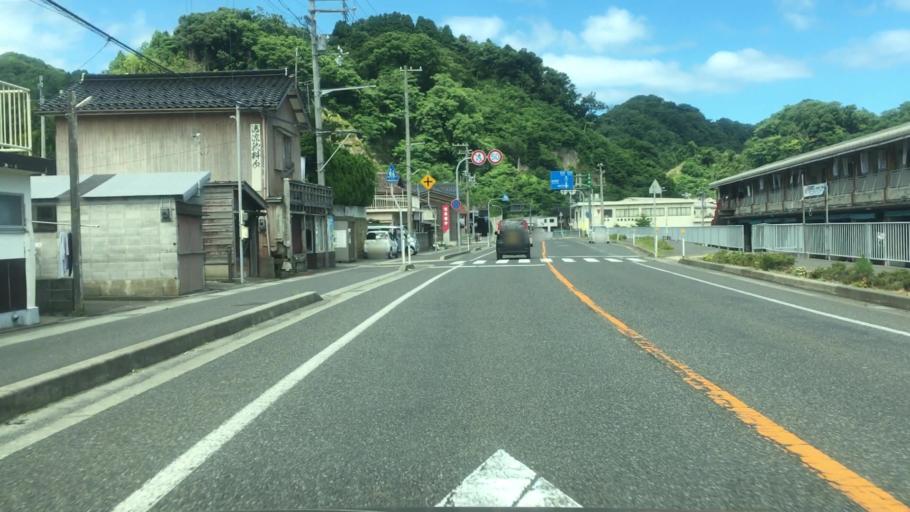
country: JP
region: Tottori
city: Tottori
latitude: 35.6199
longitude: 134.4311
